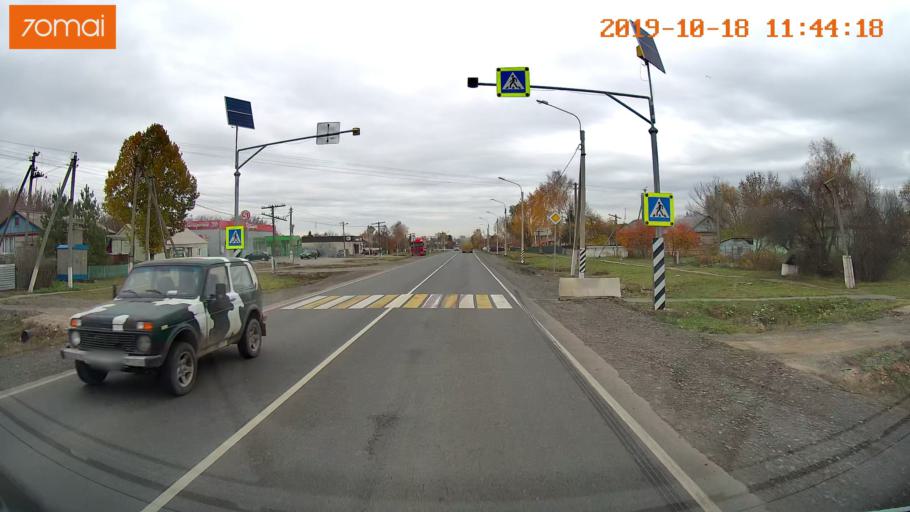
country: RU
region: Rjazan
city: Oktyabr'skiy
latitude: 54.2016
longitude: 38.9555
